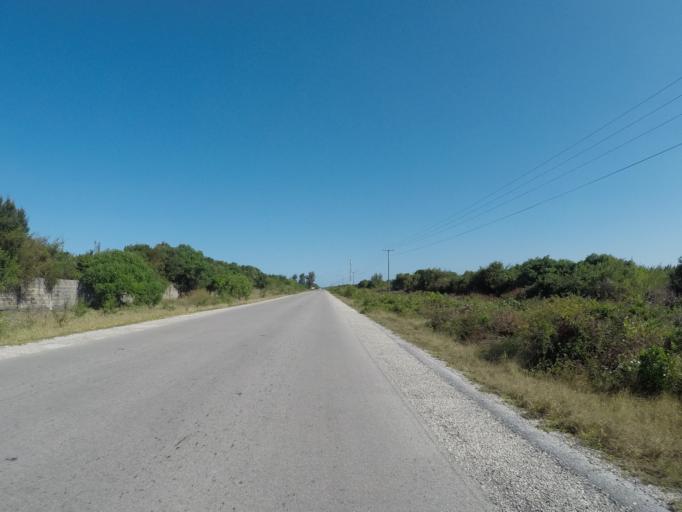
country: TZ
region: Zanzibar Central/South
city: Nganane
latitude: -6.1728
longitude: 39.5265
